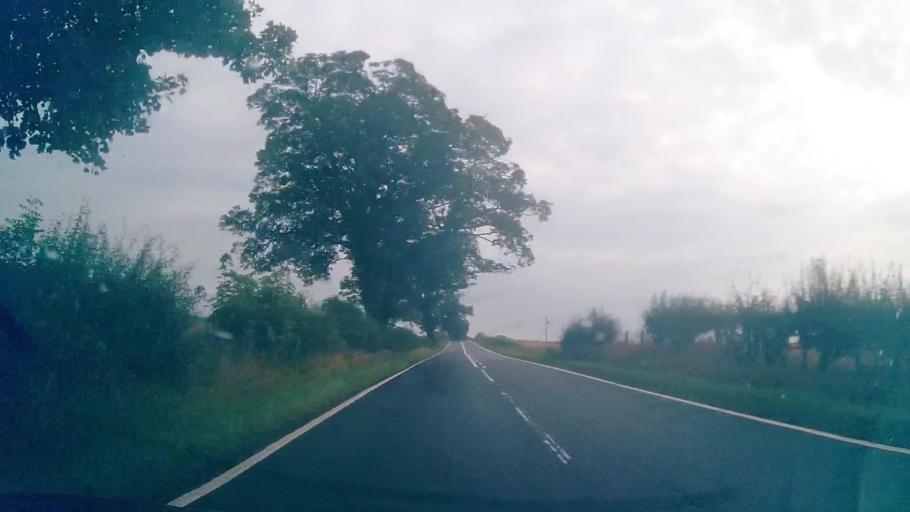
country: GB
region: Scotland
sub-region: Dumfries and Galloway
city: Locharbriggs
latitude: 55.0649
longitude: -3.5045
